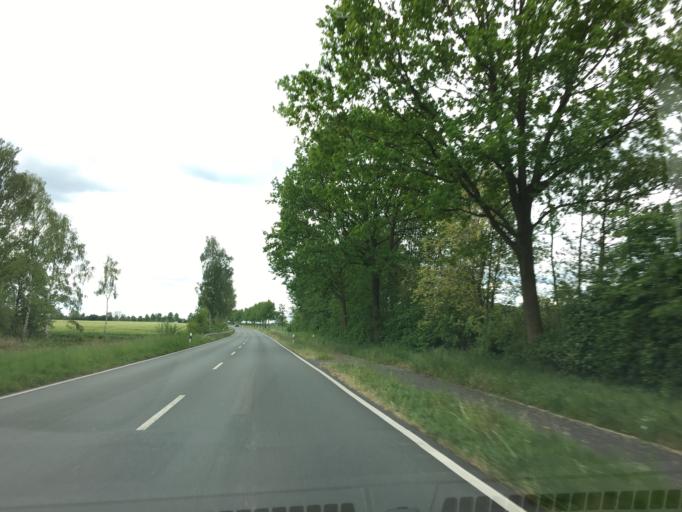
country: DE
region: North Rhine-Westphalia
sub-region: Regierungsbezirk Munster
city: Havixbeck
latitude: 51.9303
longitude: 7.4529
